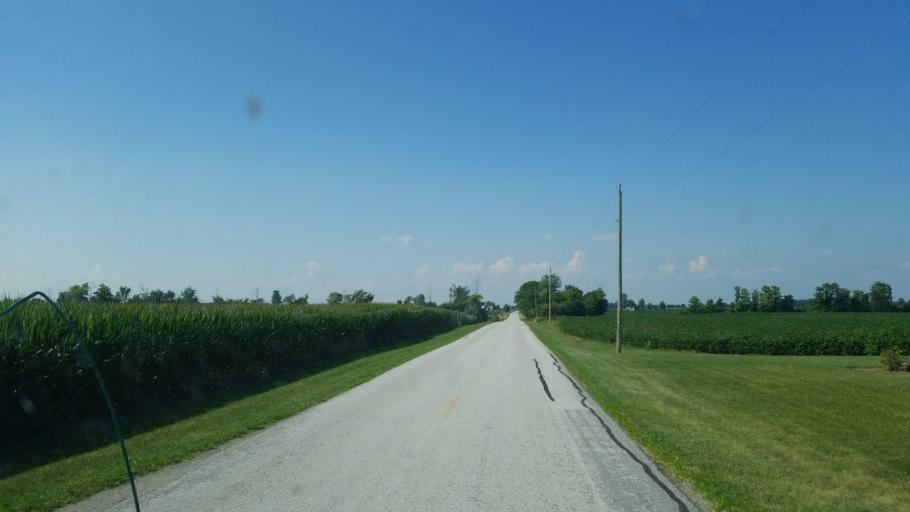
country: US
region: Ohio
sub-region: Hardin County
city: Forest
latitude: 40.6997
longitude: -83.4958
